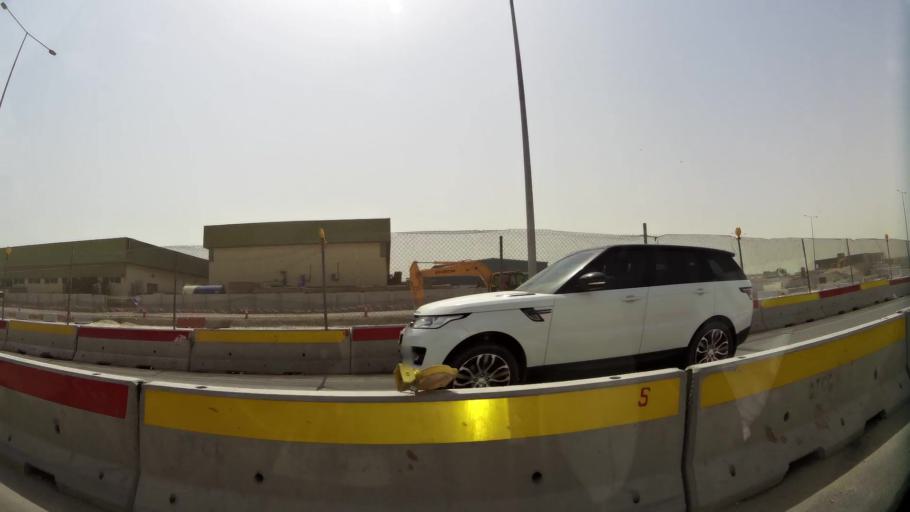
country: QA
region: Baladiyat ar Rayyan
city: Ar Rayyan
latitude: 25.2069
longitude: 51.4101
